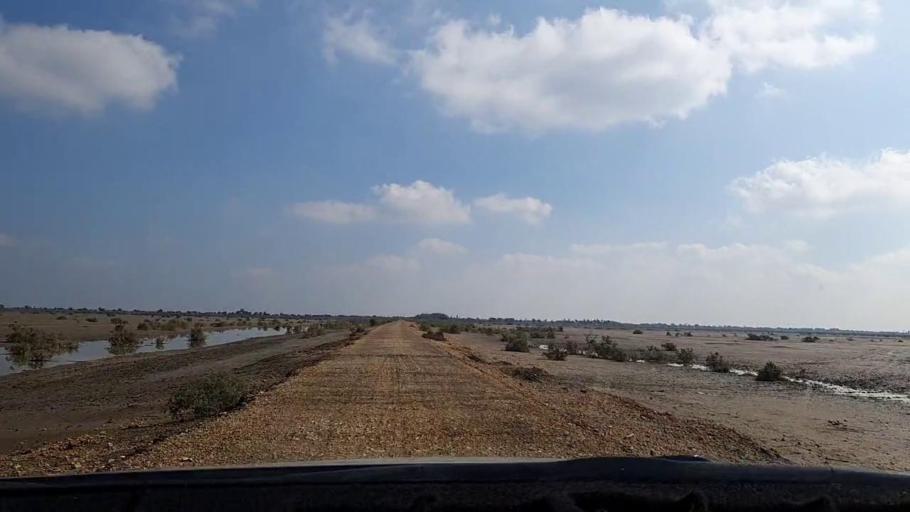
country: PK
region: Sindh
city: Pithoro
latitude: 25.7366
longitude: 69.2781
